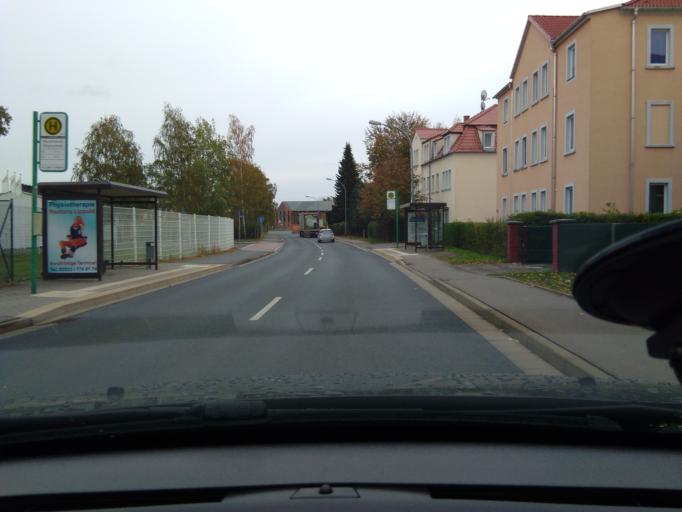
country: DE
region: Saxony
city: Niederau
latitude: 51.1475
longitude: 13.5378
